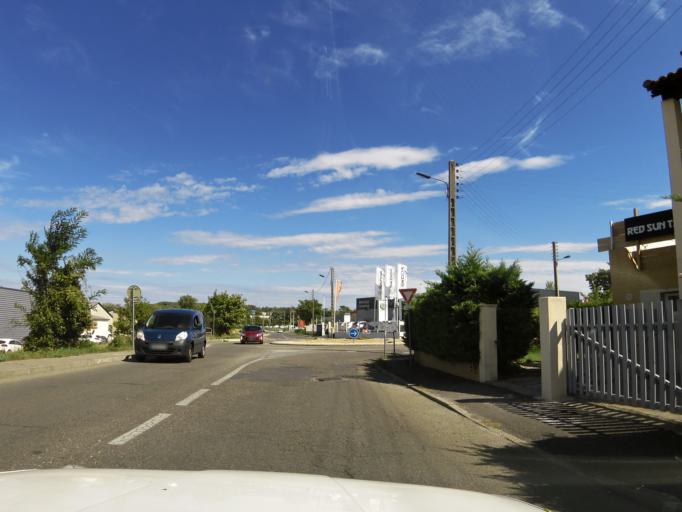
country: FR
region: Languedoc-Roussillon
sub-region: Departement du Gard
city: Ales
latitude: 44.1382
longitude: 4.0953
